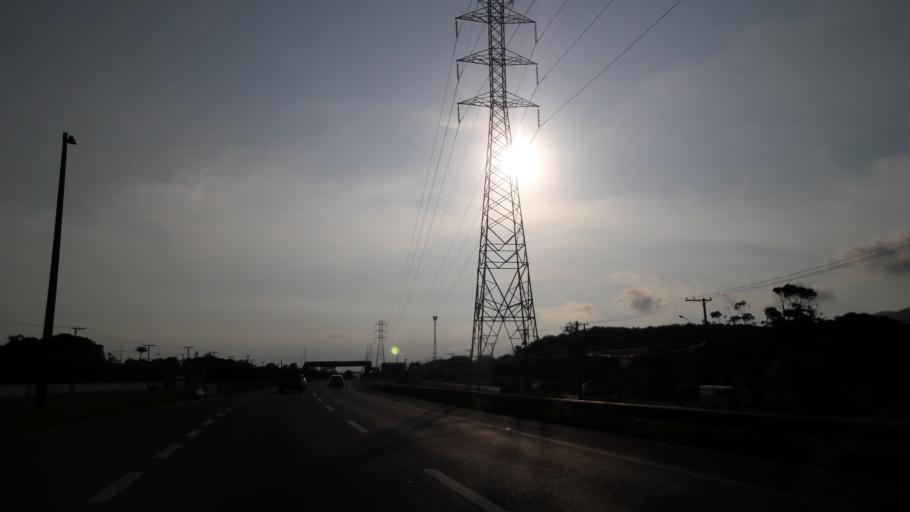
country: BR
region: Sao Paulo
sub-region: Itanhaem
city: Itanhaem
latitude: -24.1406
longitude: -46.7134
